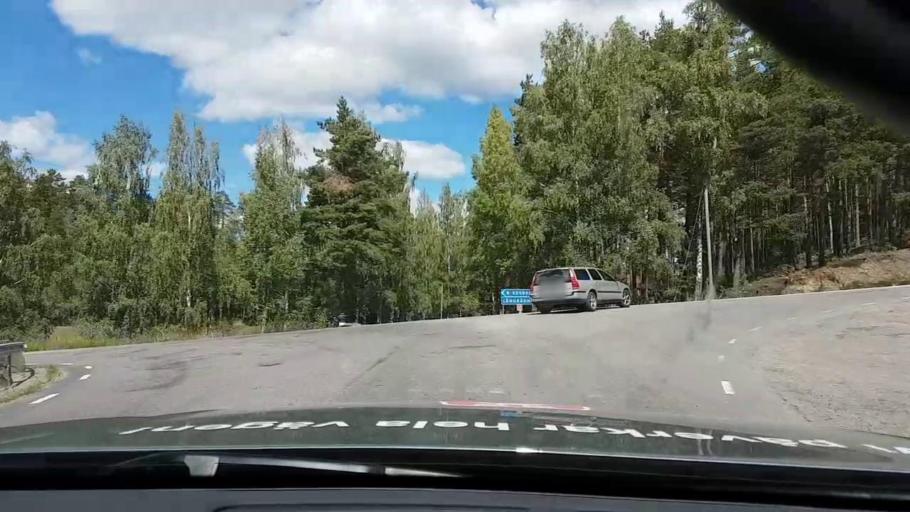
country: SE
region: Kalmar
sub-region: Vasterviks Kommun
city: Forserum
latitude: 58.0248
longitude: 16.5732
